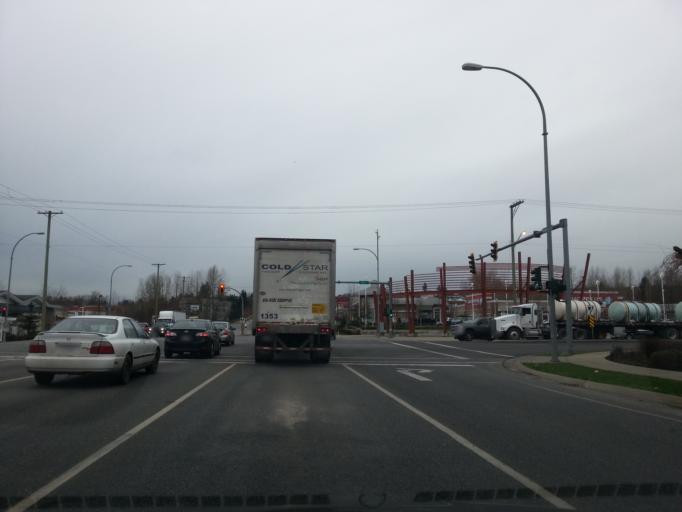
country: CA
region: British Columbia
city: Surrey
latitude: 49.1045
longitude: -122.8007
